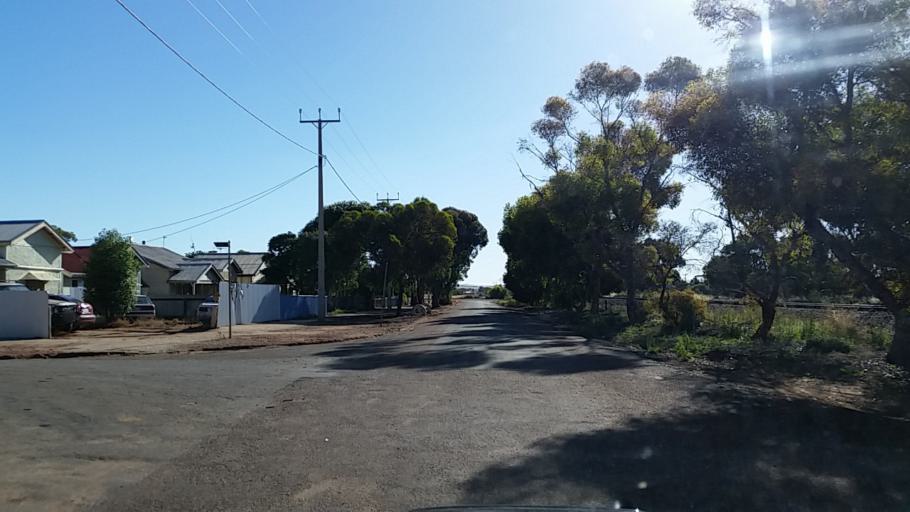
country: AU
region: South Australia
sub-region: Peterborough
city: Peterborough
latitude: -32.9780
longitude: 138.8220
